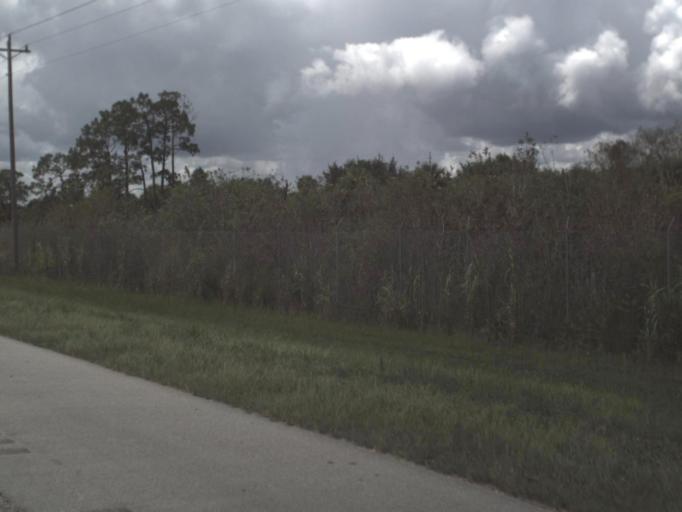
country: US
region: Florida
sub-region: Collier County
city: Immokalee
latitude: 26.1551
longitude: -81.3241
